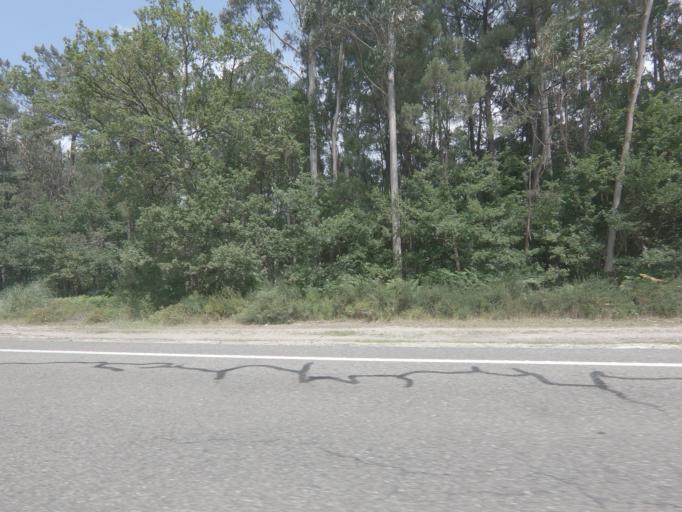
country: ES
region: Galicia
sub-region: Provincia de Pontevedra
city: Tomino
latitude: 42.0191
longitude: -8.7324
